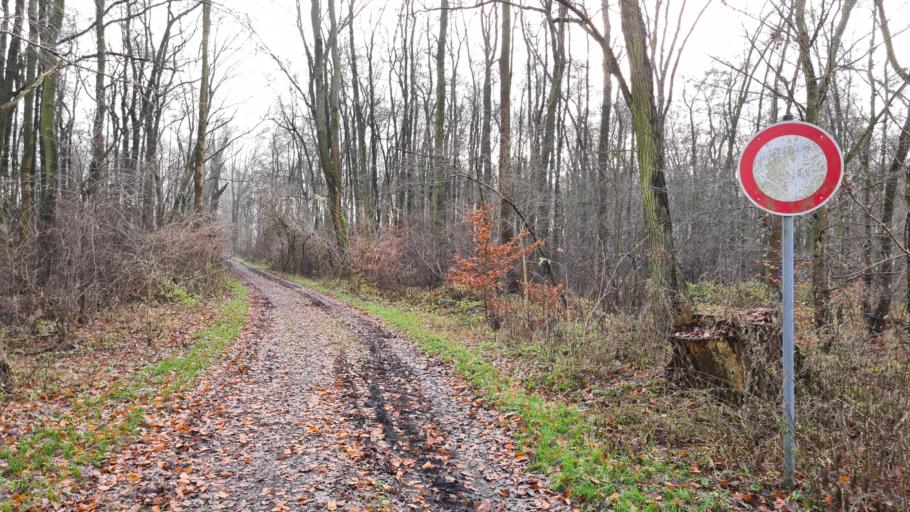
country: DE
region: Brandenburg
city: Schonewalde
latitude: 51.6981
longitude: 13.5979
